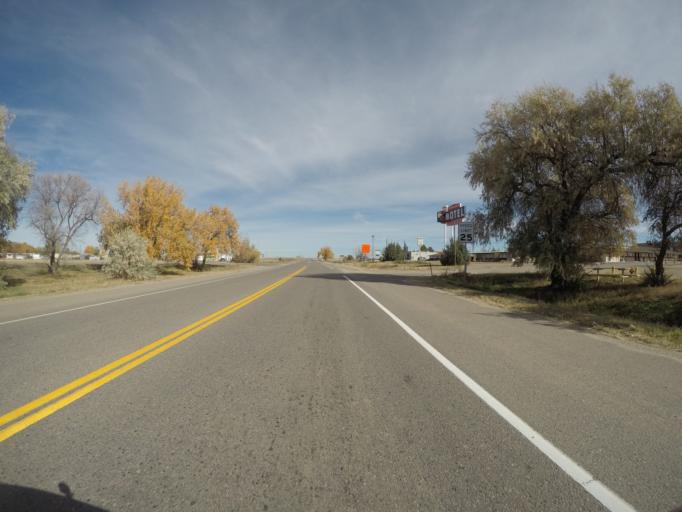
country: US
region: Colorado
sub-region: Arapahoe County
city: Byers
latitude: 39.7169
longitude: -104.2209
